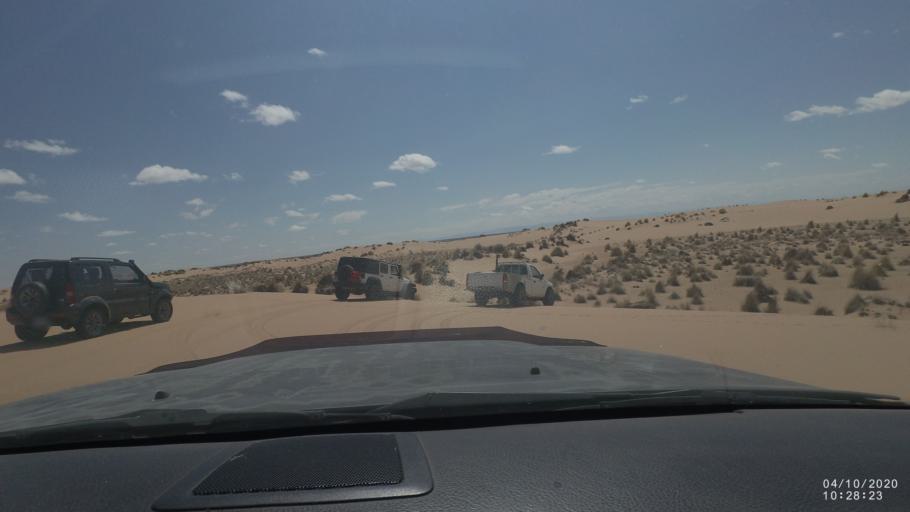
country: BO
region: Oruro
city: Poopo
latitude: -18.7037
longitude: -67.4864
